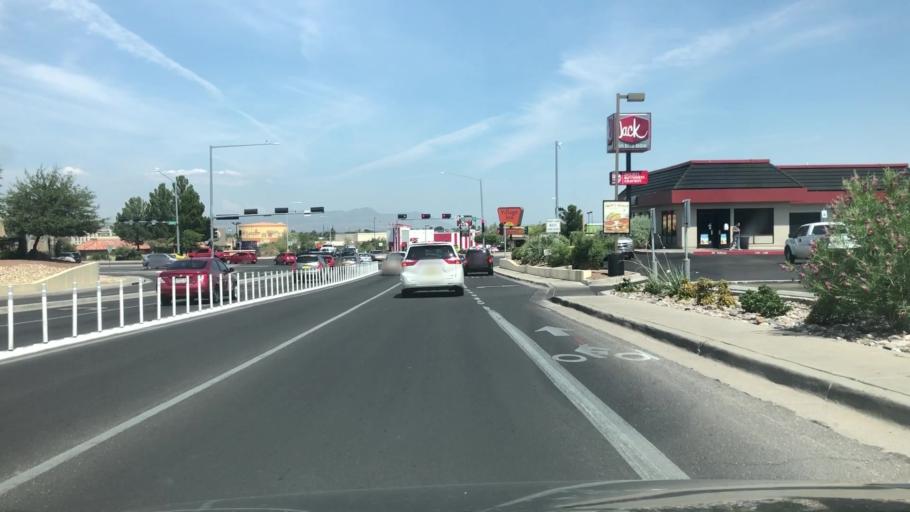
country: US
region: New Mexico
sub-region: Dona Ana County
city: University Park
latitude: 32.3147
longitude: -106.7438
